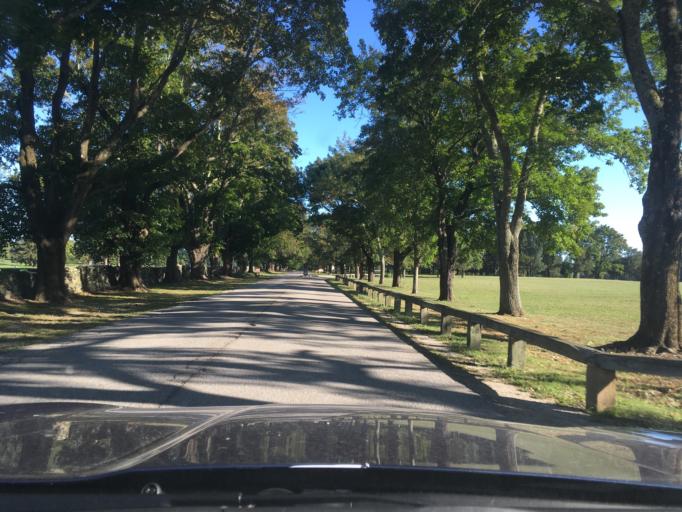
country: US
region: Rhode Island
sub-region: Kent County
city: East Greenwich
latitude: 41.6619
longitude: -71.4326
